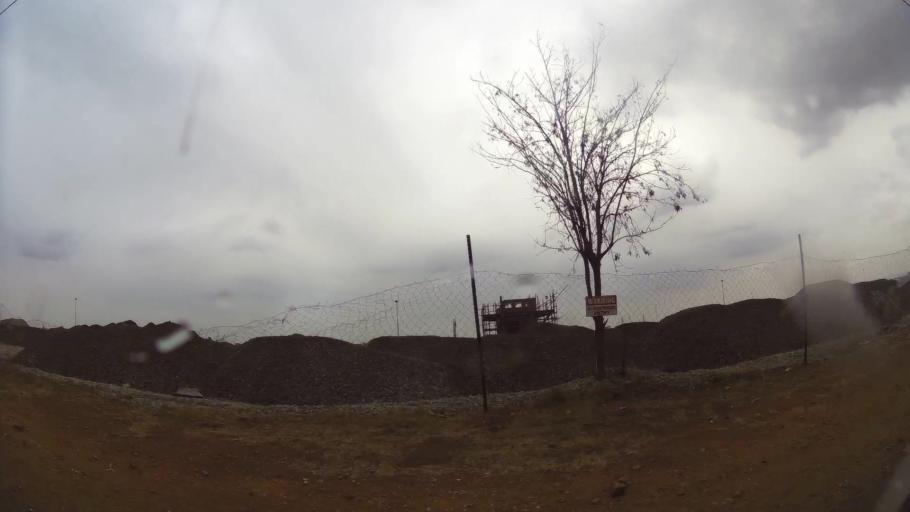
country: ZA
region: Gauteng
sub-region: Ekurhuleni Metropolitan Municipality
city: Germiston
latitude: -26.3539
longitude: 28.1441
